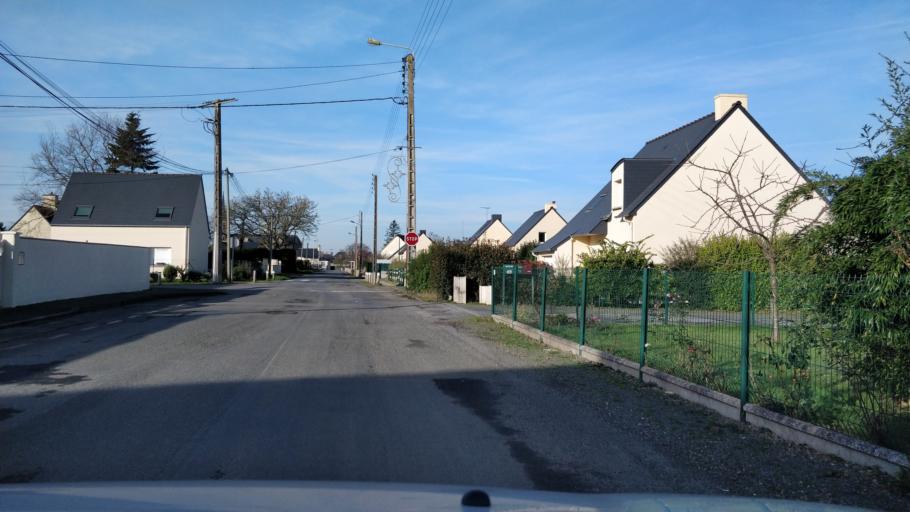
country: FR
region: Brittany
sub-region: Departement d'Ille-et-Vilaine
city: Plerguer
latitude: 48.5248
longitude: -1.8440
